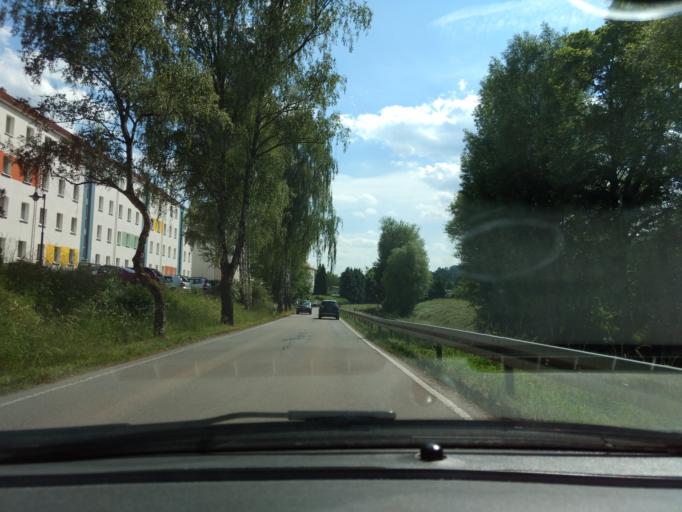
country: DE
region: Saxony
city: Dippoldiswalde
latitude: 50.9035
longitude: 13.6661
